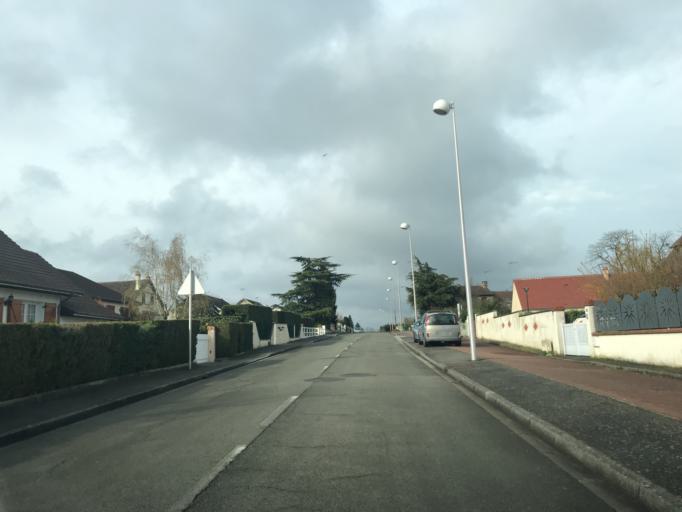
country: FR
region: Centre
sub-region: Departement du Loiret
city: Saint-Martin-sur-Ocre
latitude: 47.6808
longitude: 2.6544
